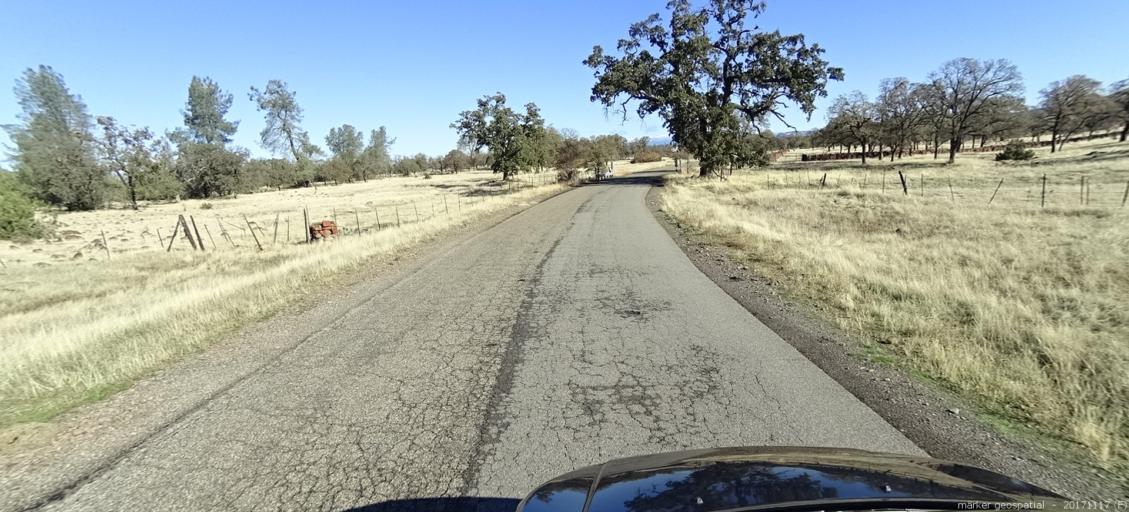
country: US
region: California
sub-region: Shasta County
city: Palo Cedro
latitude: 40.4526
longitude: -122.1102
